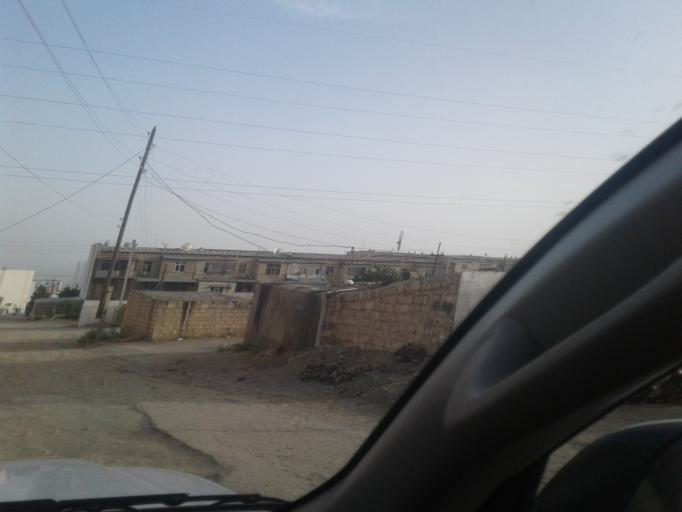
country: TM
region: Balkan
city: Turkmenbasy
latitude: 40.0069
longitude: 52.9651
